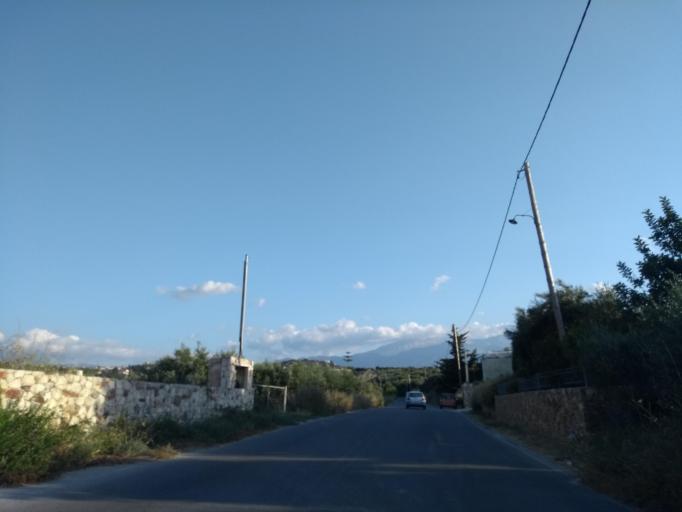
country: GR
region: Crete
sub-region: Nomos Chanias
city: Kalivai
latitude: 35.4433
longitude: 24.1762
